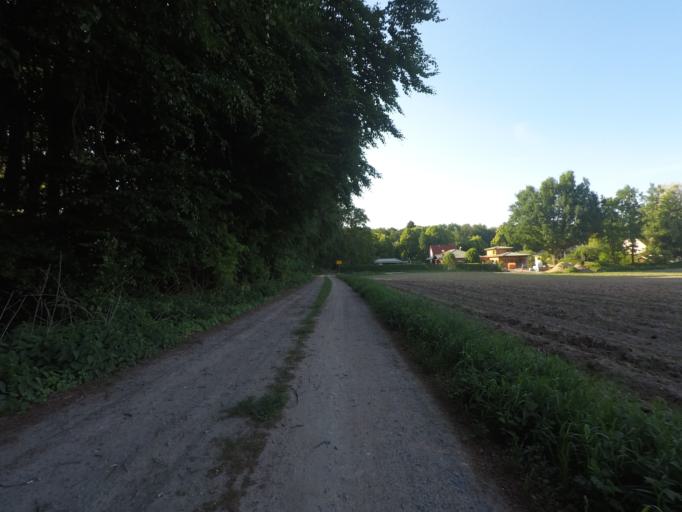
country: DE
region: Brandenburg
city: Joachimsthal
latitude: 52.9044
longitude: 13.7014
